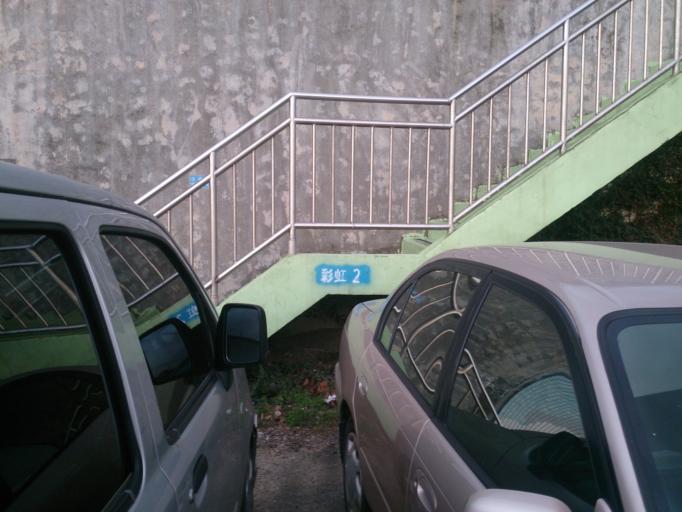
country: TW
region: Taipei
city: Taipei
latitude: 25.0553
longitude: 121.5736
